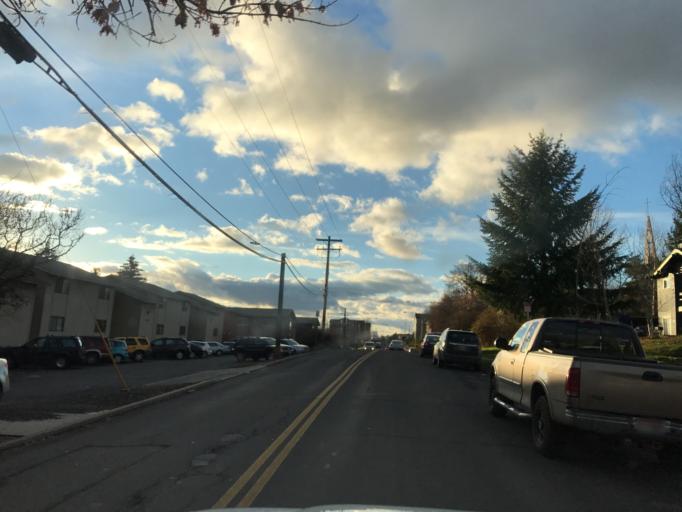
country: US
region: Idaho
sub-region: Latah County
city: Moscow
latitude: 46.7346
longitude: -117.0138
